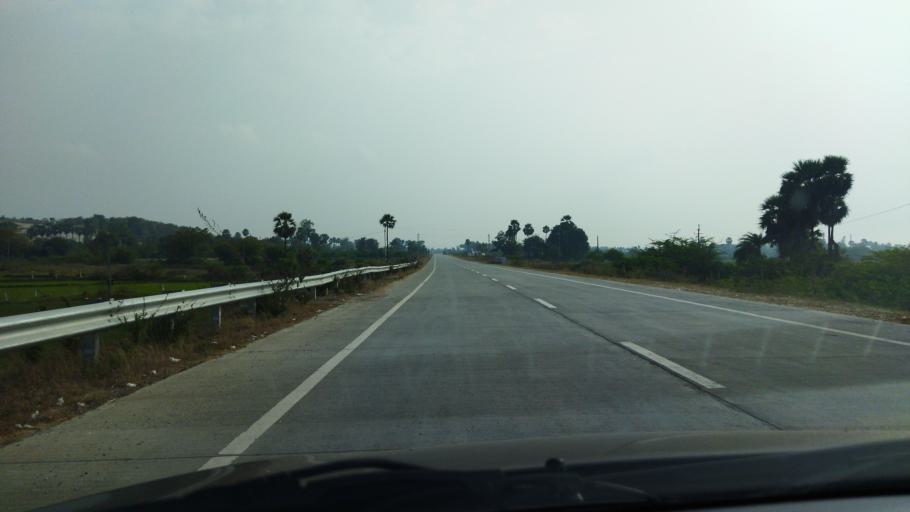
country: IN
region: Telangana
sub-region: Nalgonda
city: Nalgonda
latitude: 17.1803
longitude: 79.4097
